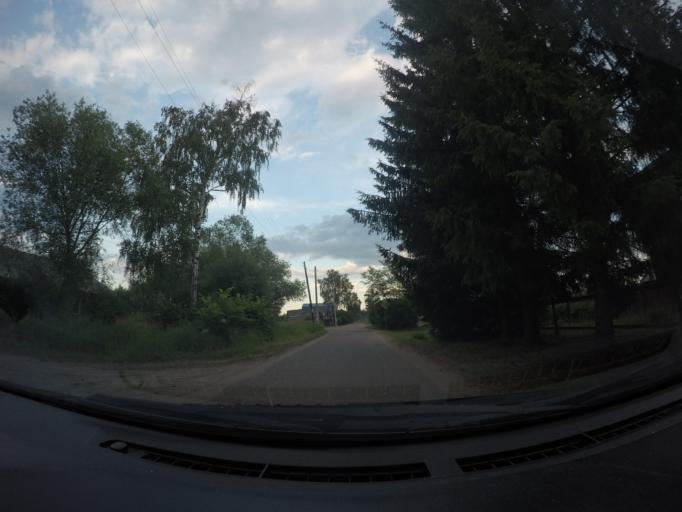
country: RU
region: Moskovskaya
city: Krasnyy Tkach
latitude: 55.4241
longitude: 39.2422
